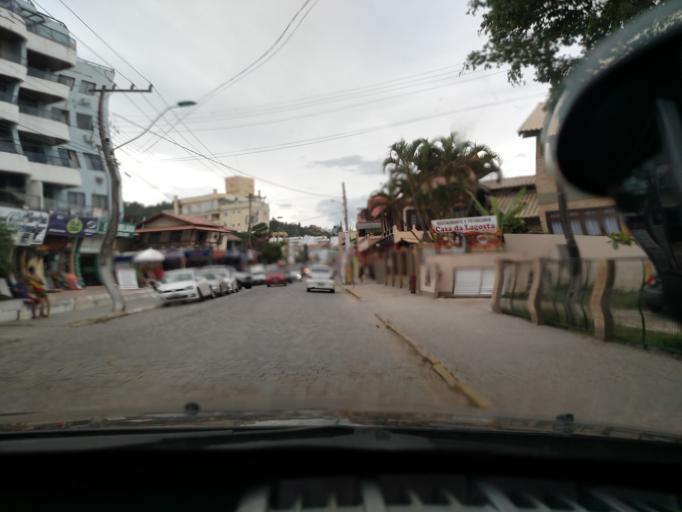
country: BR
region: Santa Catarina
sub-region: Porto Belo
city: Porto Belo
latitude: -27.1494
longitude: -48.4859
